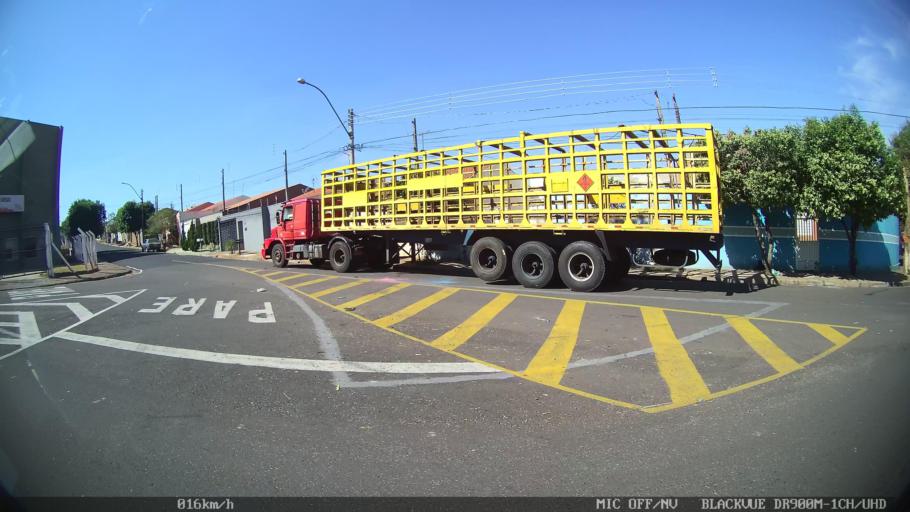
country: BR
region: Sao Paulo
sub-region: Sao Jose Do Rio Preto
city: Sao Jose do Rio Preto
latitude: -20.7828
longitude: -49.4157
